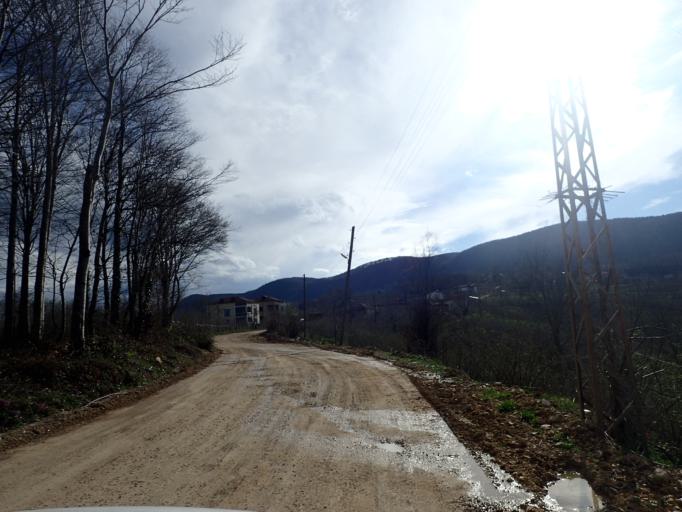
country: TR
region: Ordu
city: Kumru
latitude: 40.9317
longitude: 37.2550
